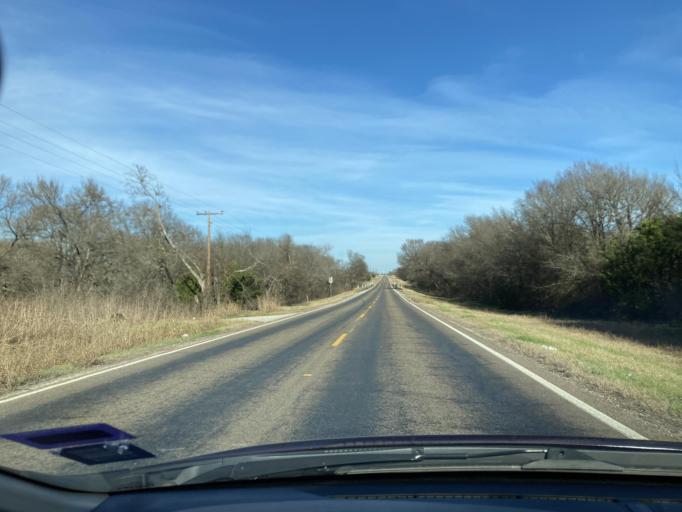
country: US
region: Texas
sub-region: Navarro County
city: Corsicana
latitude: 32.0118
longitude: -96.4299
